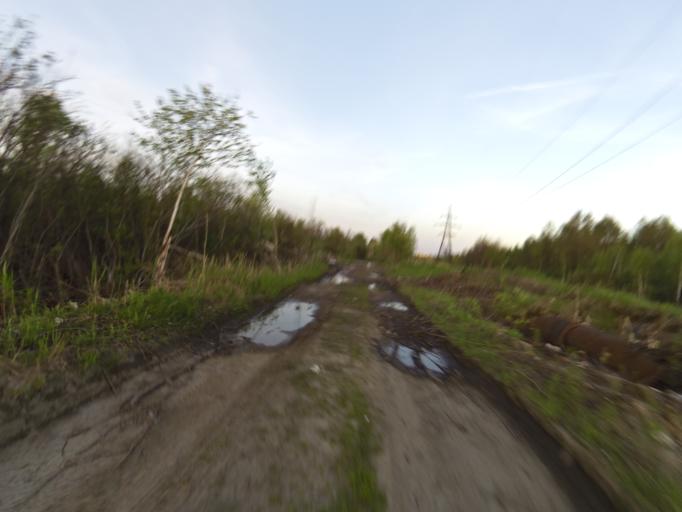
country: RU
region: Sverdlovsk
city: Shirokaya Rechka
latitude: 56.8416
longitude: 60.5014
